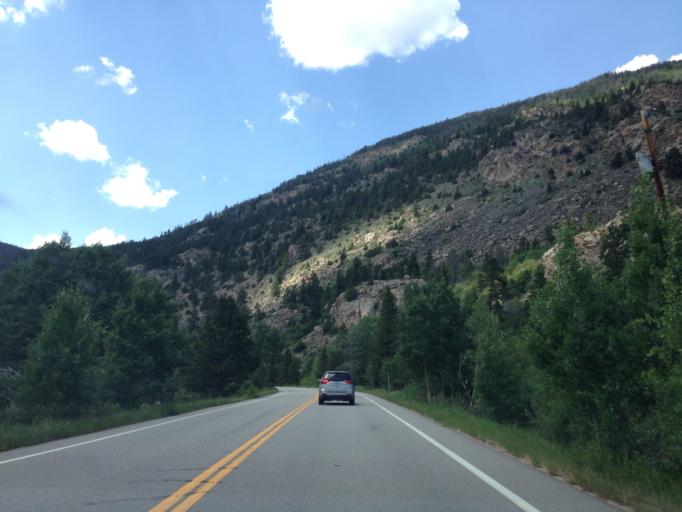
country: US
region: Colorado
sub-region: Larimer County
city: Estes Park
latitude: 40.6709
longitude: -105.7985
